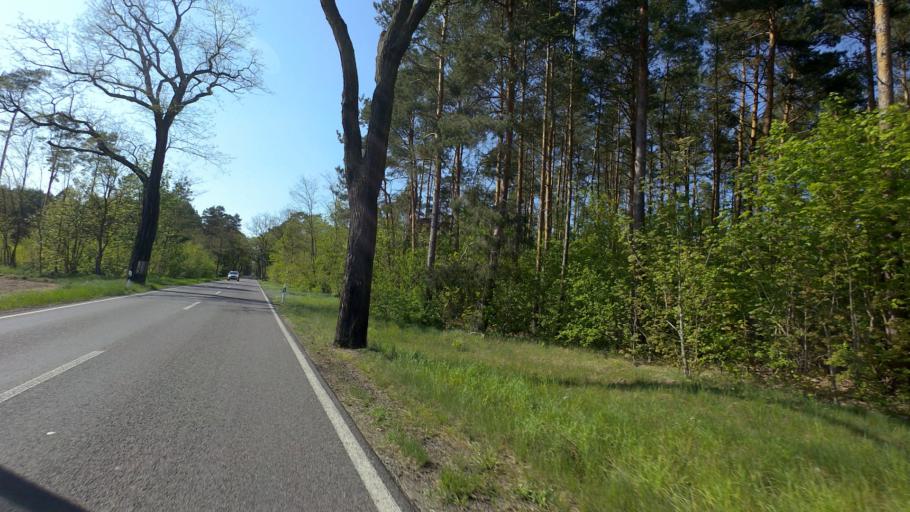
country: DE
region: Brandenburg
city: Munchehofe
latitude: 52.1050
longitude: 13.7893
